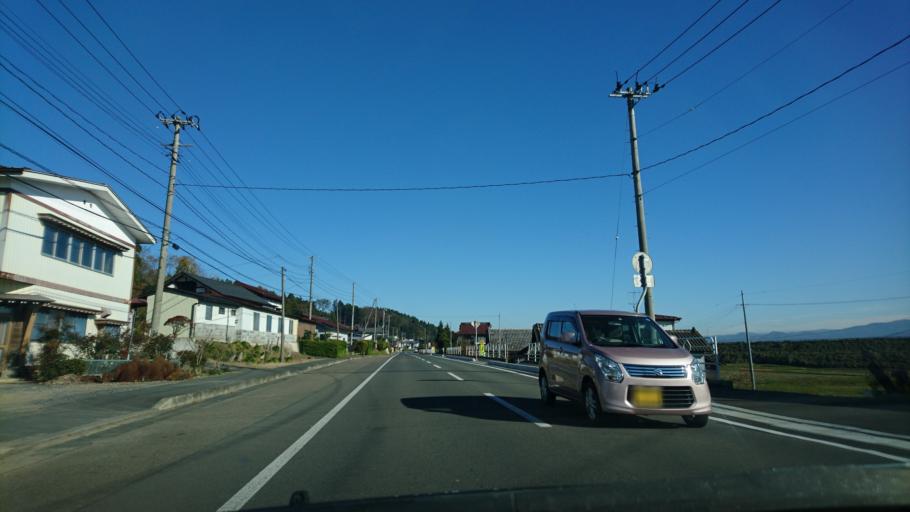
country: JP
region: Iwate
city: Mizusawa
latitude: 39.0691
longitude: 141.1285
